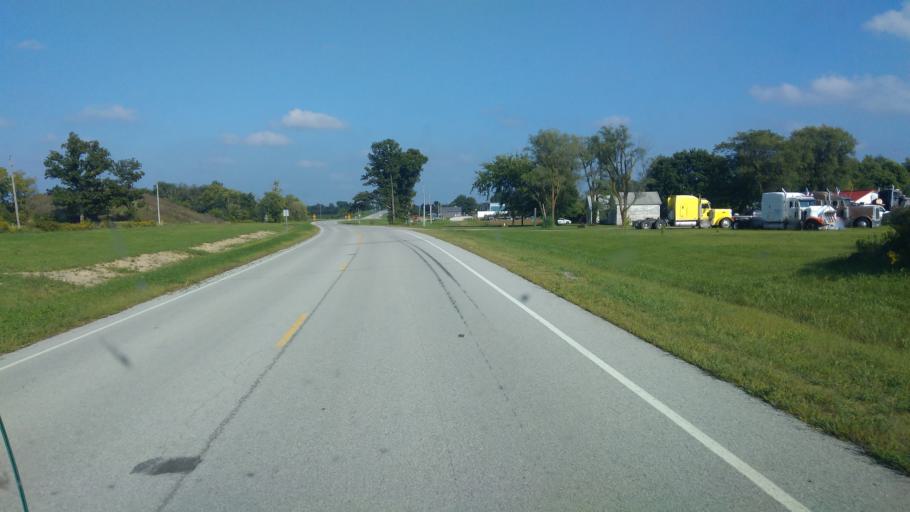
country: US
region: Ohio
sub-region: Hancock County
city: Arlington
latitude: 40.8342
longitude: -83.6571
